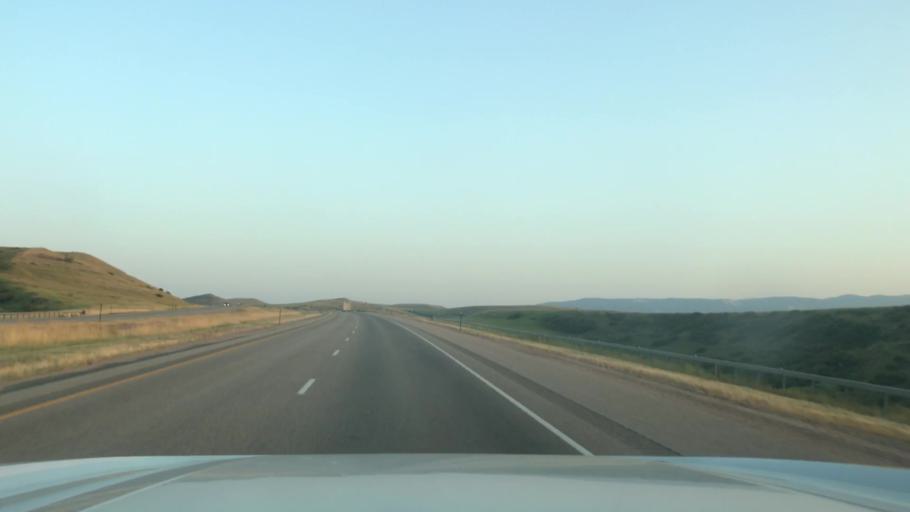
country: US
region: Wyoming
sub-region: Sheridan County
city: Sheridan
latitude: 44.7252
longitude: -106.9185
